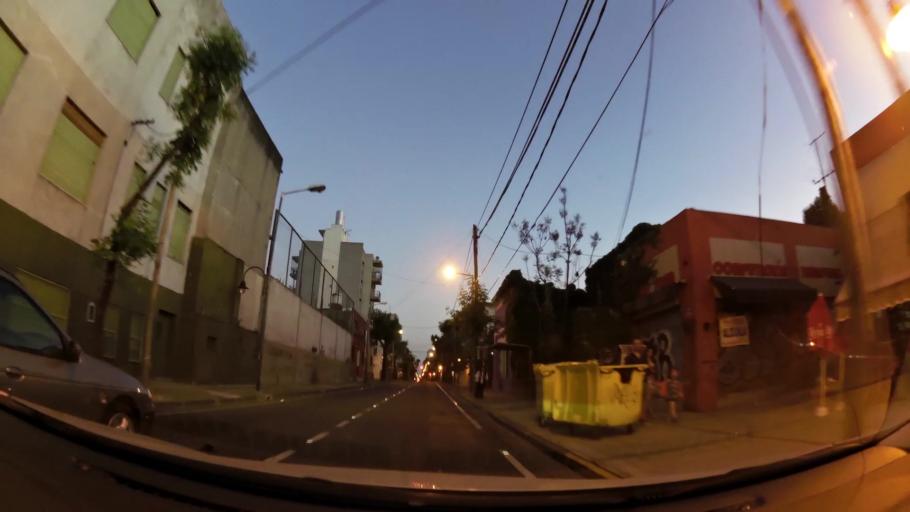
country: AR
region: Buenos Aires
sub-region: Partido de Tigre
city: Tigre
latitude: -34.4369
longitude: -58.5604
